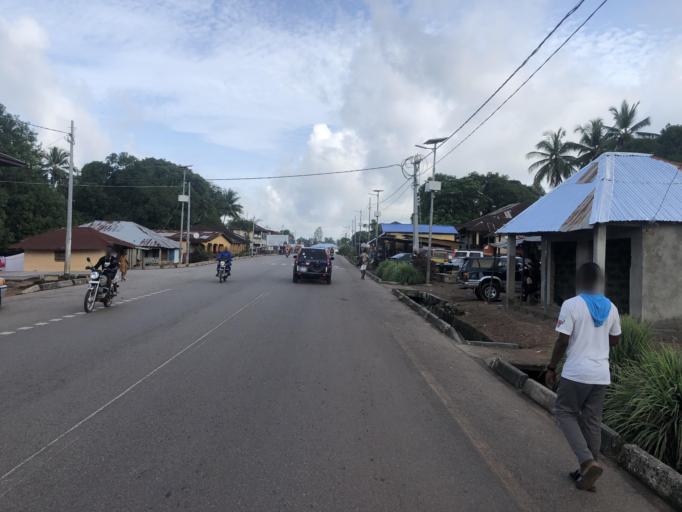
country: SL
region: Northern Province
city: Magburaka
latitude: 8.7217
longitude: -11.9441
